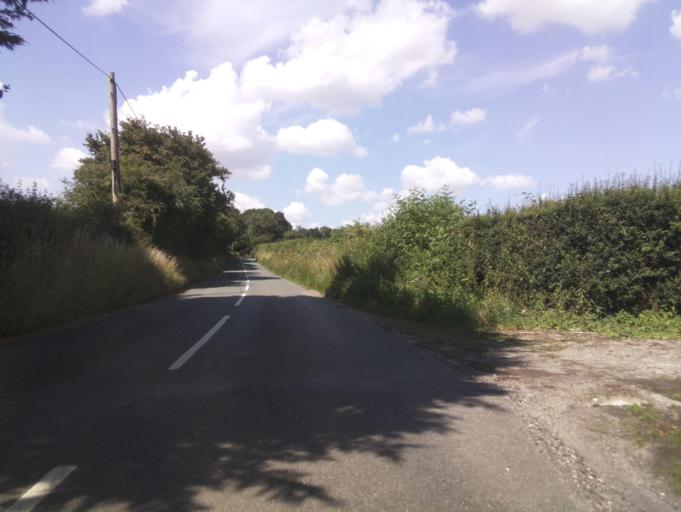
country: GB
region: England
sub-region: West Berkshire
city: Farnborough
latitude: 51.4908
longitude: -1.3655
